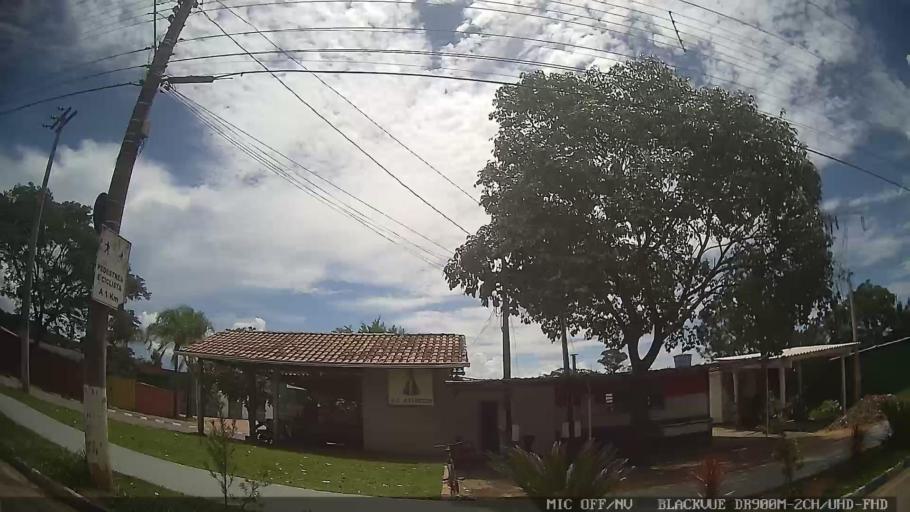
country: BR
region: Sao Paulo
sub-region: Conchas
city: Conchas
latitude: -23.0831
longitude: -47.9757
